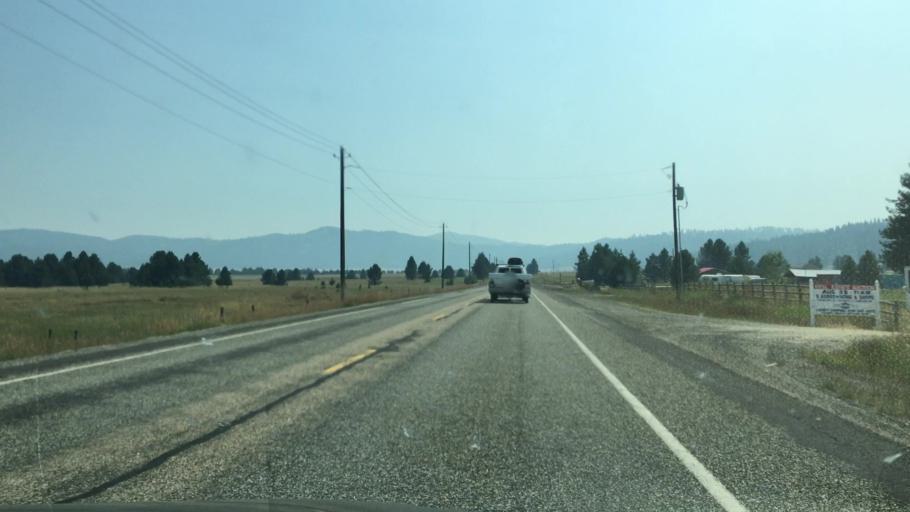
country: US
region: Idaho
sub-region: Valley County
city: Cascade
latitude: 44.3584
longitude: -116.0220
